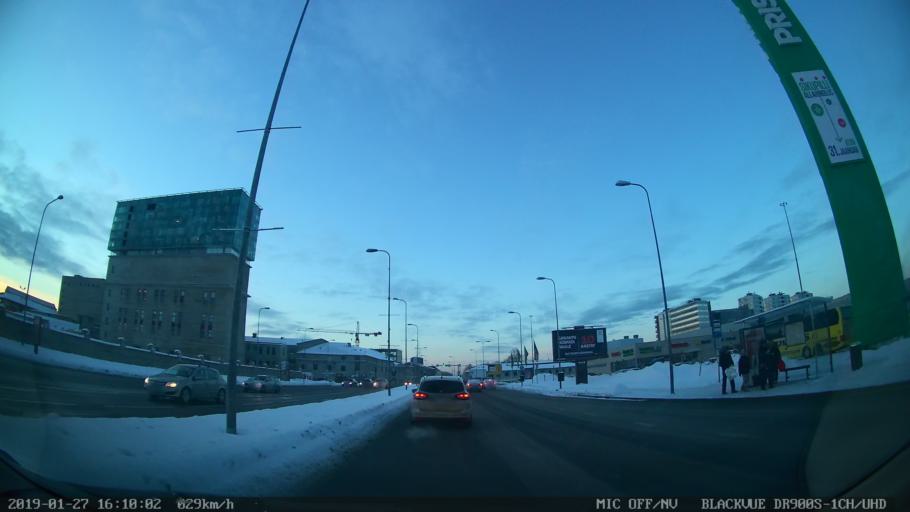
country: EE
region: Harju
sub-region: Tallinna linn
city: Tallinn
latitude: 59.4252
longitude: 24.7833
